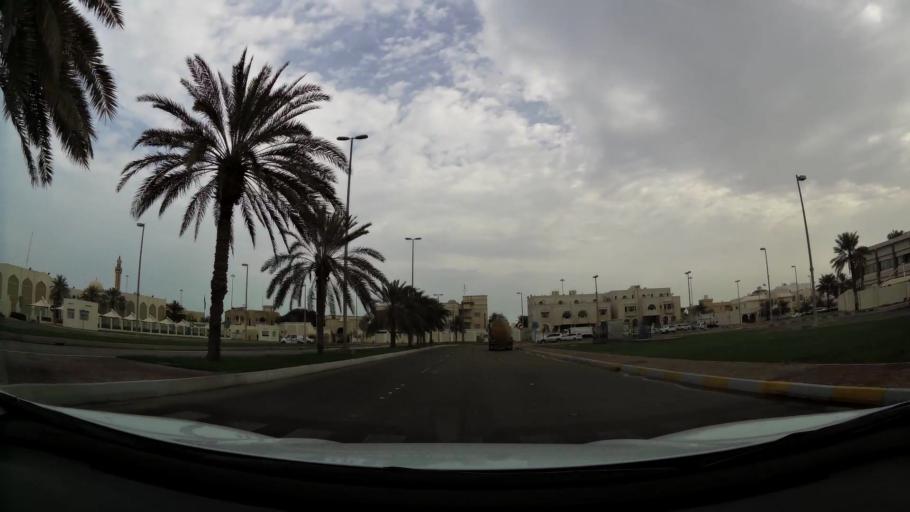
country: AE
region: Abu Dhabi
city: Abu Dhabi
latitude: 24.4483
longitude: 54.4056
